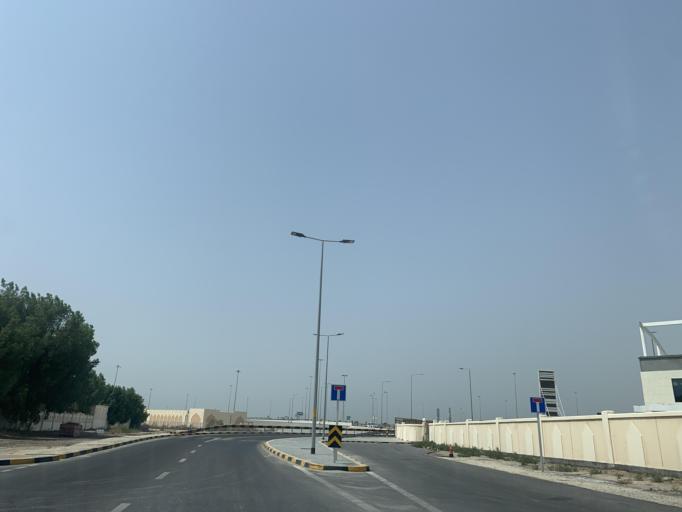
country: BH
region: Central Governorate
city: Madinat Hamad
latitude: 26.1683
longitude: 50.4653
